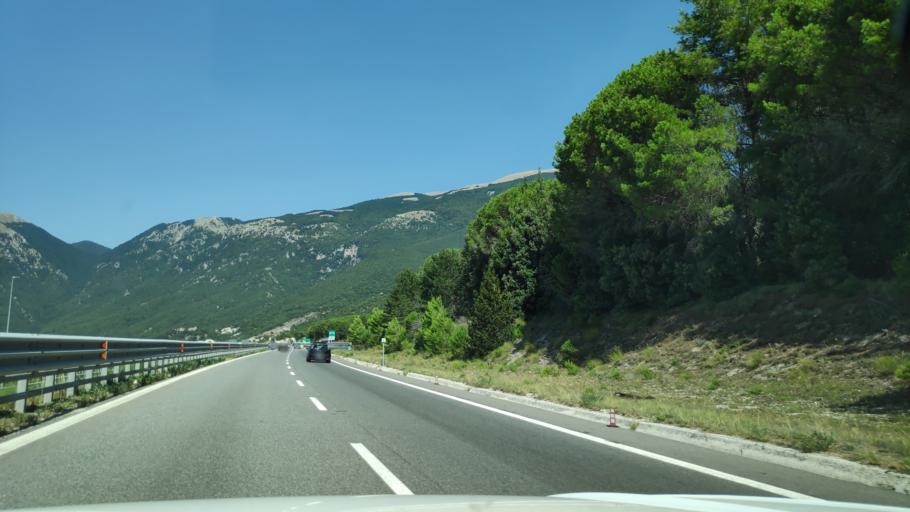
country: IT
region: Calabria
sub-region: Provincia di Cosenza
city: Morano Calabro
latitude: 39.8754
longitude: 16.1676
